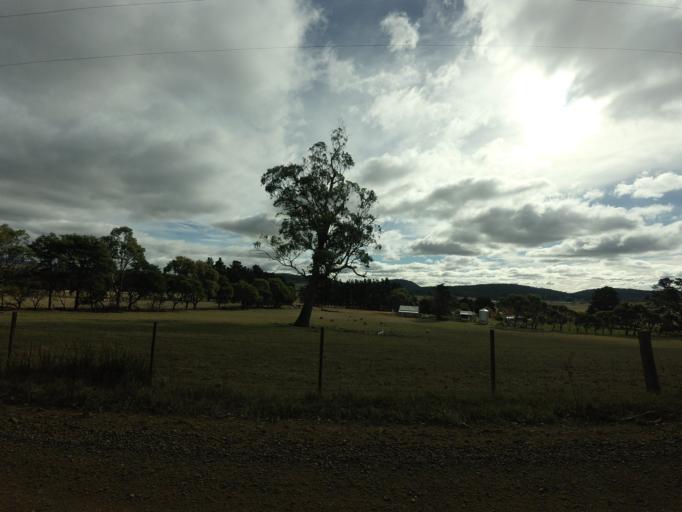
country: AU
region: Tasmania
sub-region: Brighton
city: Bridgewater
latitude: -42.4117
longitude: 147.3992
